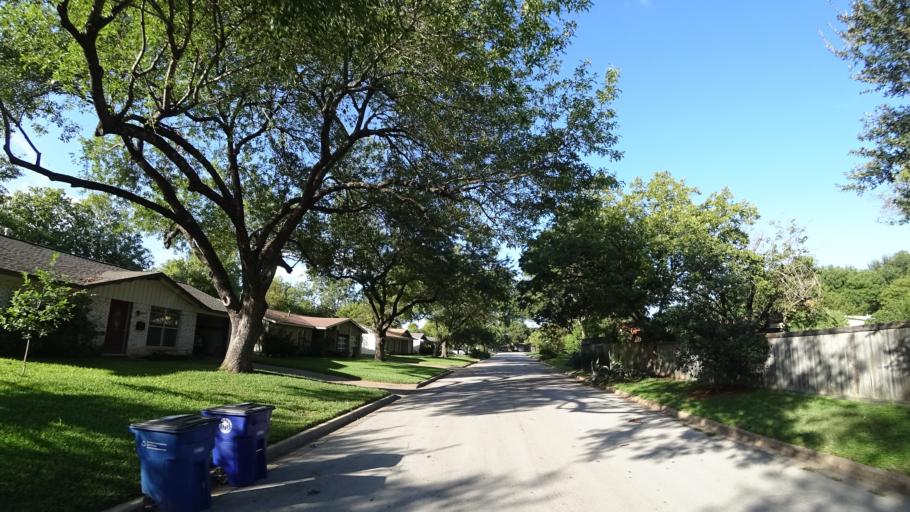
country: US
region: Texas
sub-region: Williamson County
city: Jollyville
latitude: 30.3633
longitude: -97.7373
